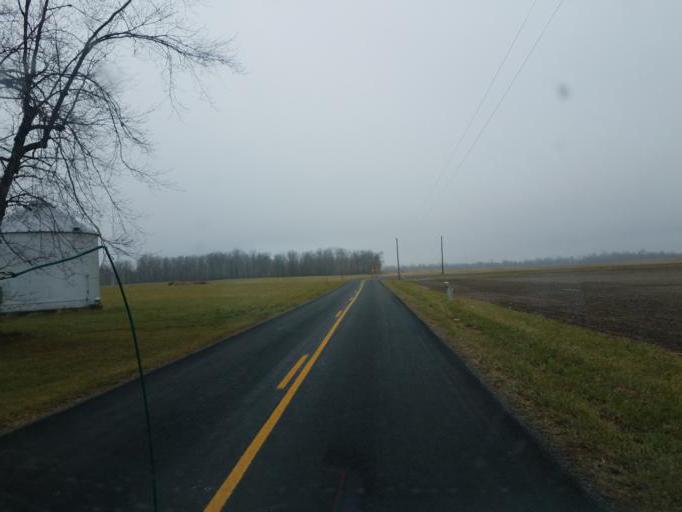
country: US
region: Ohio
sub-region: Champaign County
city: North Lewisburg
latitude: 40.2404
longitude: -83.5471
